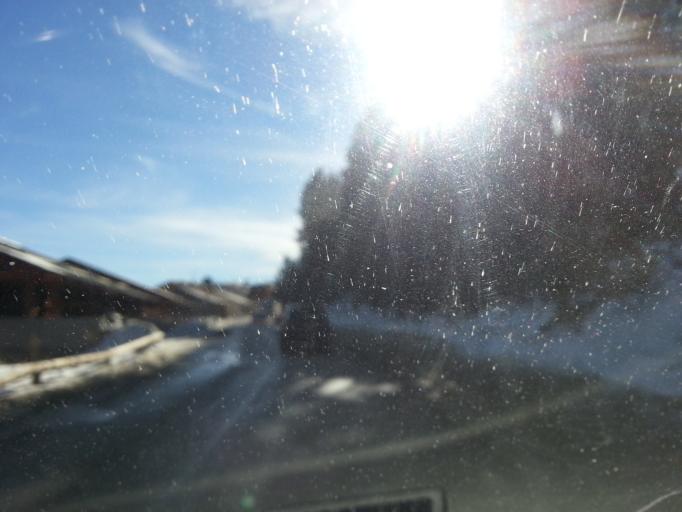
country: ES
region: Catalonia
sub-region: Provincia de Girona
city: Llivia
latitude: 42.5687
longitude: 2.0697
